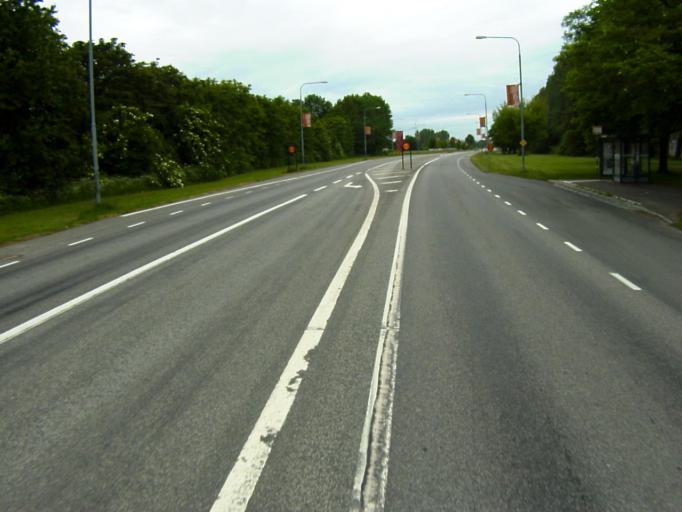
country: SE
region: Skane
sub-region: Kristianstads Kommun
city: Kristianstad
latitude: 56.0540
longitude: 14.1619
